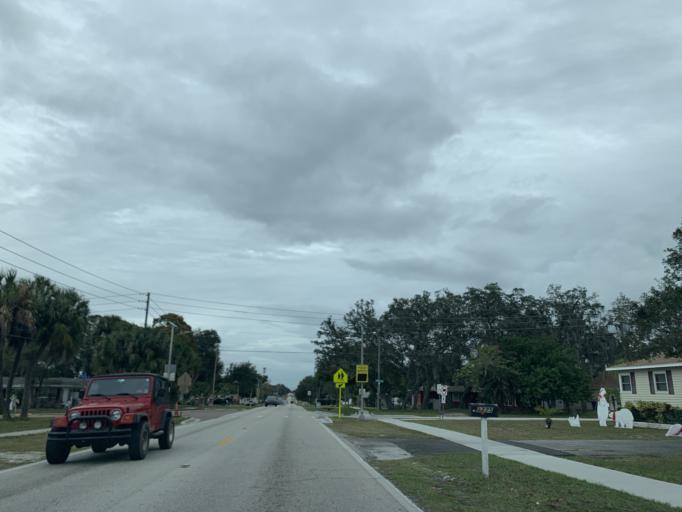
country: US
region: Florida
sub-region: Pinellas County
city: Belleair
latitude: 27.9389
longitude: -82.7838
